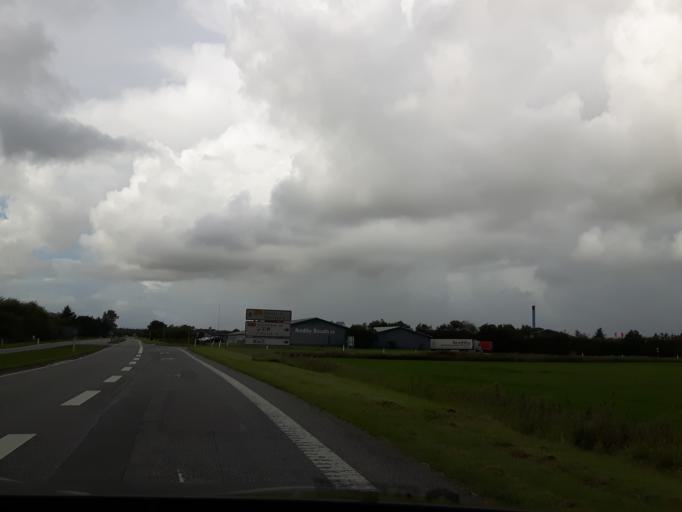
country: DK
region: North Denmark
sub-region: Thisted Kommune
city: Thisted
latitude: 57.0309
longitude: 8.8629
